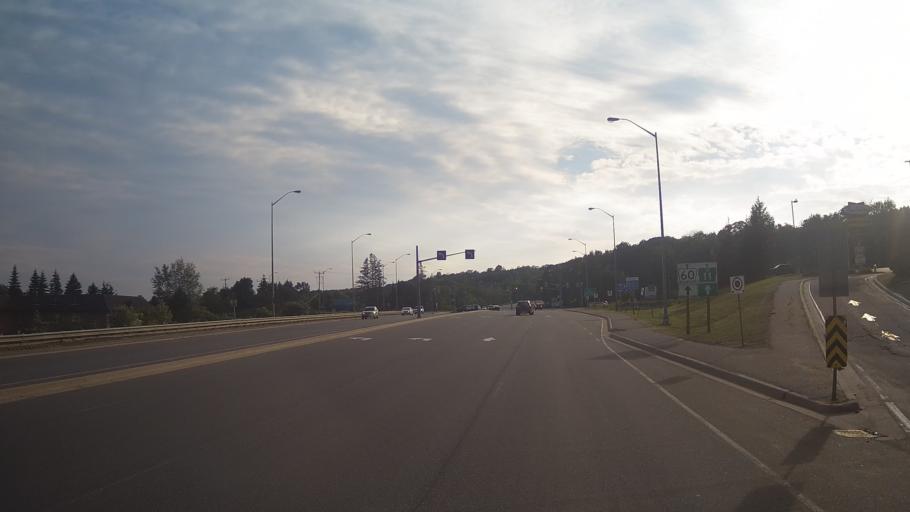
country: CA
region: Ontario
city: Huntsville
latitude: 45.3375
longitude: -79.2009
